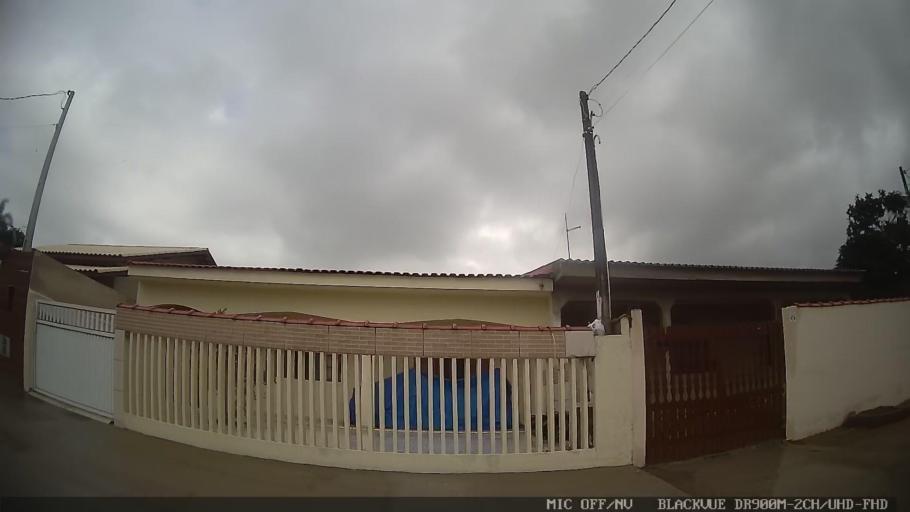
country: BR
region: Sao Paulo
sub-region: Itanhaem
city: Itanhaem
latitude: -24.1877
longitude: -46.8189
